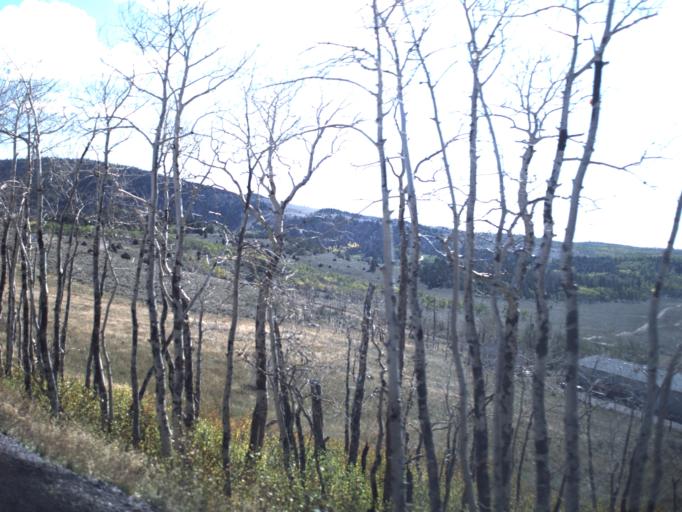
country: US
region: Utah
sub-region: Wayne County
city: Loa
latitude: 38.5138
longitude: -111.7774
